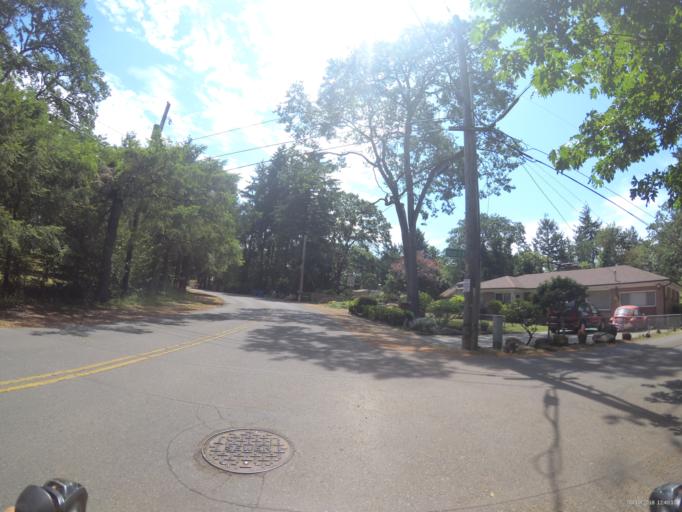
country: US
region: Washington
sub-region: Pierce County
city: Lakewood
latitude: 47.1649
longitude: -122.5279
